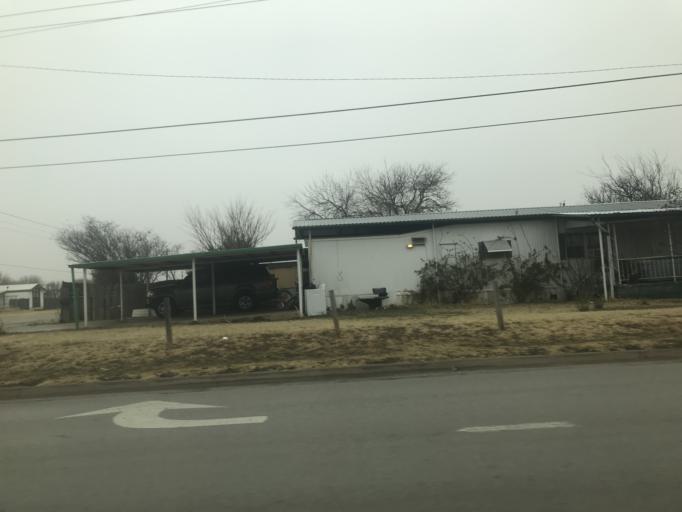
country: US
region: Texas
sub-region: Taylor County
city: Tye
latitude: 32.4434
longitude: -99.8115
